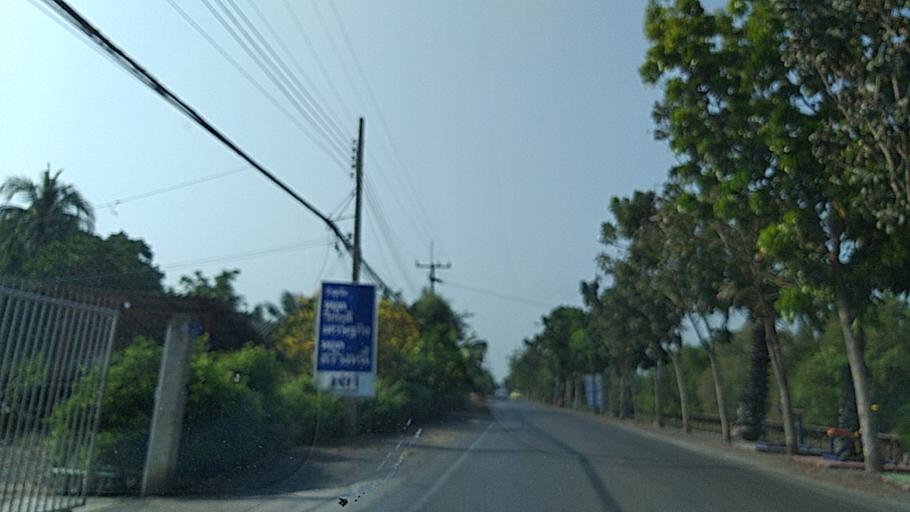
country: TH
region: Pathum Thani
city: Lam Luk Ka
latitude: 13.9482
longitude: 100.7059
